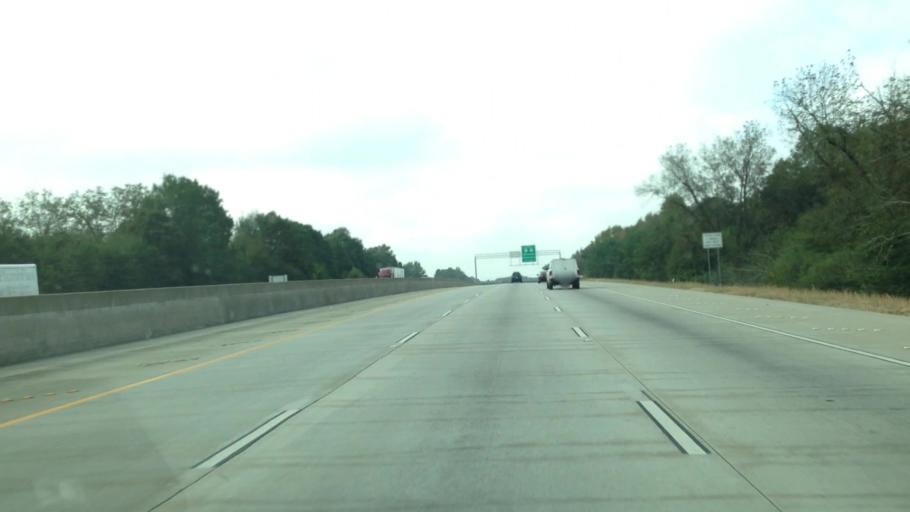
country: US
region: Georgia
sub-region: Coweta County
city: East Newnan
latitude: 33.3356
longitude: -84.7688
